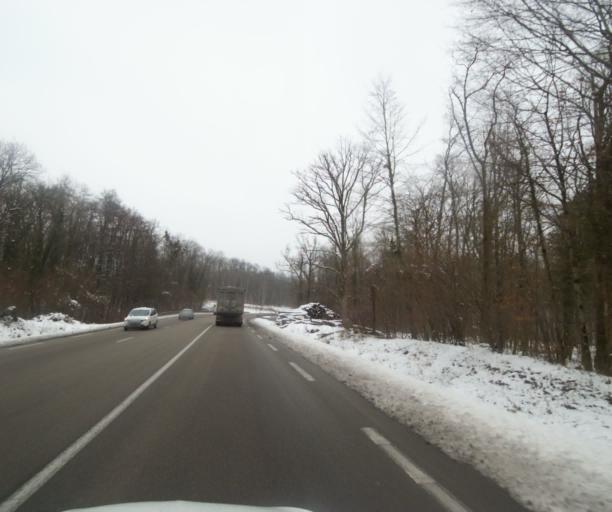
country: FR
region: Champagne-Ardenne
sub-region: Departement de la Haute-Marne
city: Saint-Dizier
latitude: 48.6094
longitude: 4.9143
